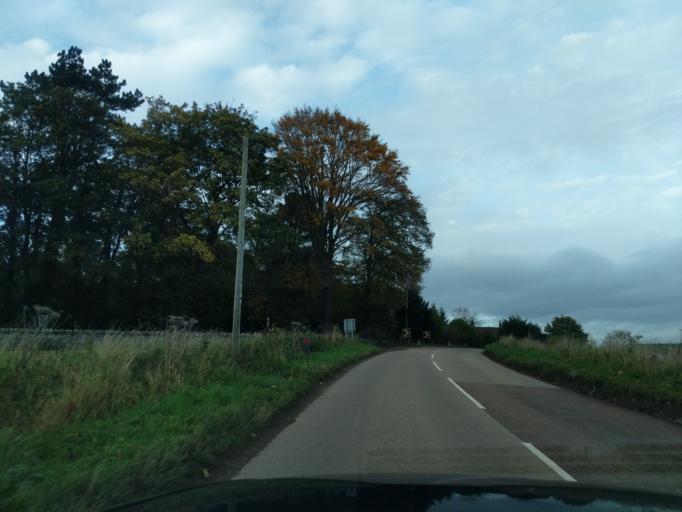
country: GB
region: Scotland
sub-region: Fife
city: Tayport
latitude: 56.4279
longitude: -2.8885
